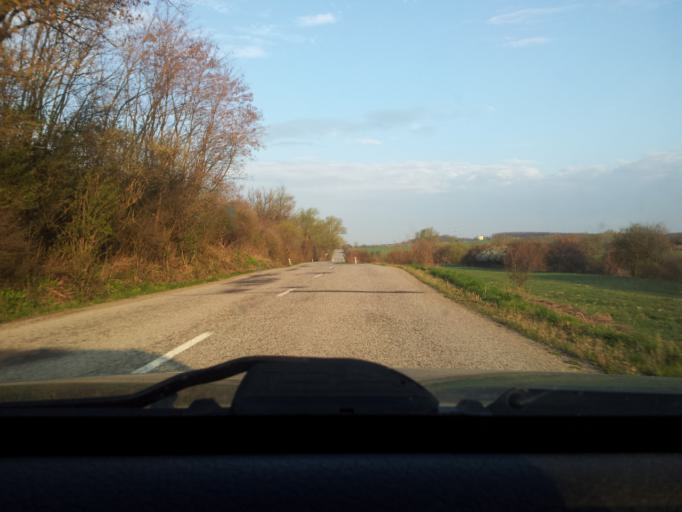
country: SK
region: Nitriansky
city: Tlmace
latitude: 48.2812
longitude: 18.4767
